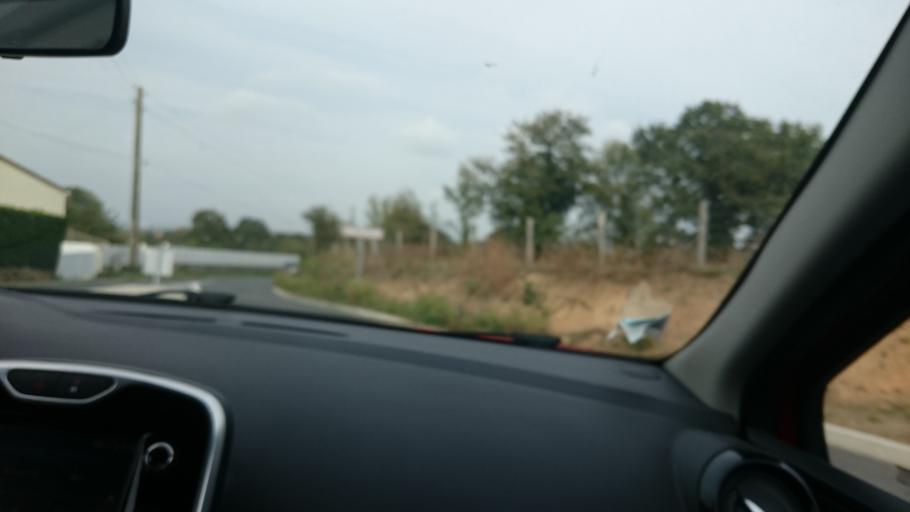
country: FR
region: Pays de la Loire
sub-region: Departement de Maine-et-Loire
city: La Tessoualle
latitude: 46.9969
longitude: -0.8425
